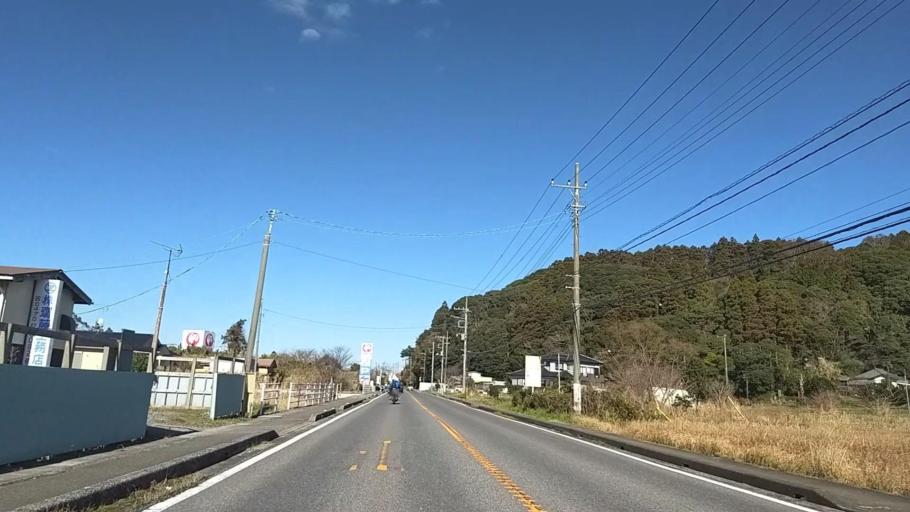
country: JP
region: Chiba
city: Ohara
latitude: 35.2250
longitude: 140.3861
